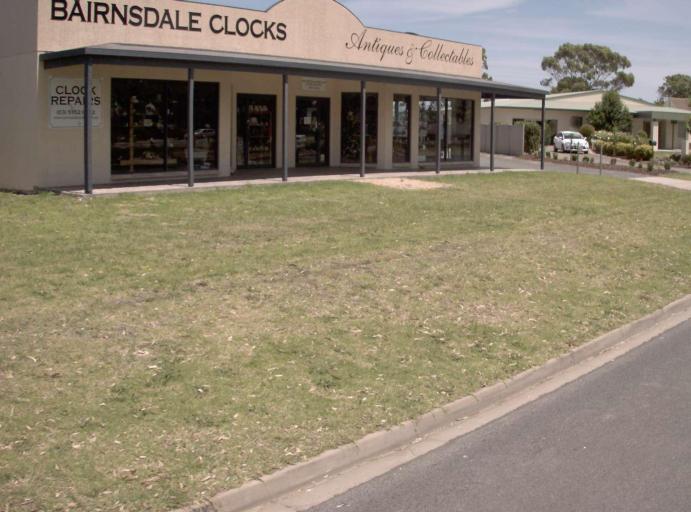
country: AU
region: Victoria
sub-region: East Gippsland
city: Bairnsdale
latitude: -37.8373
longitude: 147.5987
